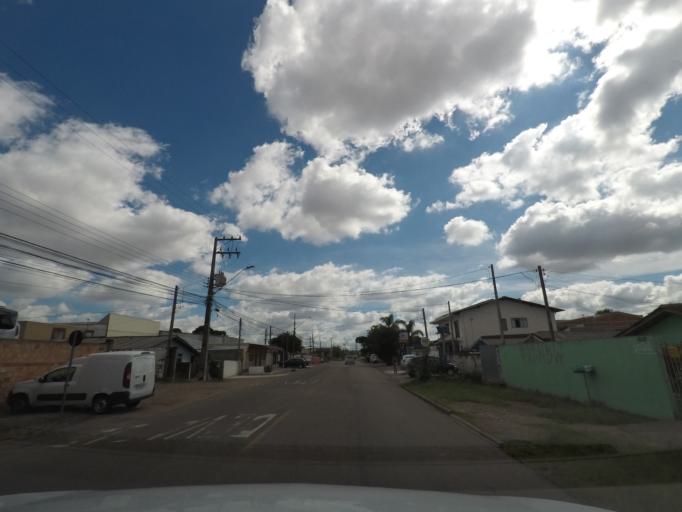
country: BR
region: Parana
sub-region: Sao Jose Dos Pinhais
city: Sao Jose dos Pinhais
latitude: -25.4967
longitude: -49.2288
